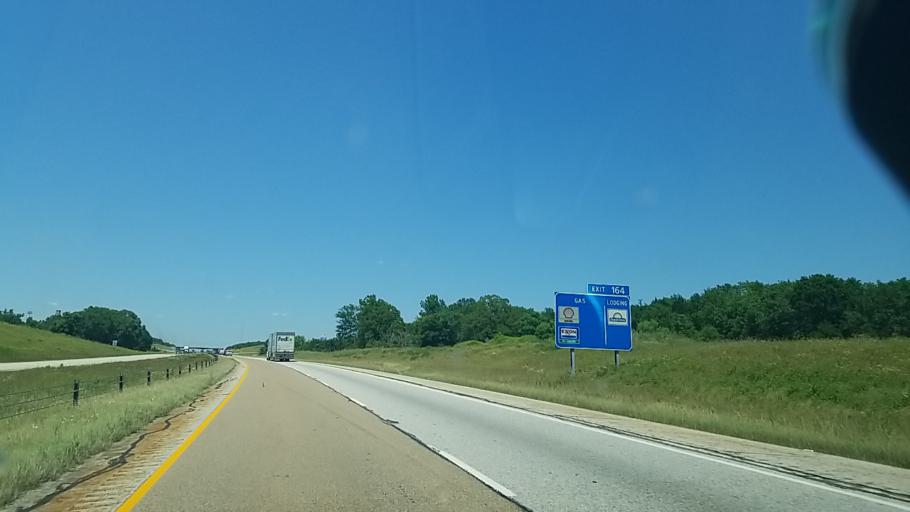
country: US
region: Texas
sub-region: Leon County
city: Centerville
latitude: 31.2488
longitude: -95.9889
